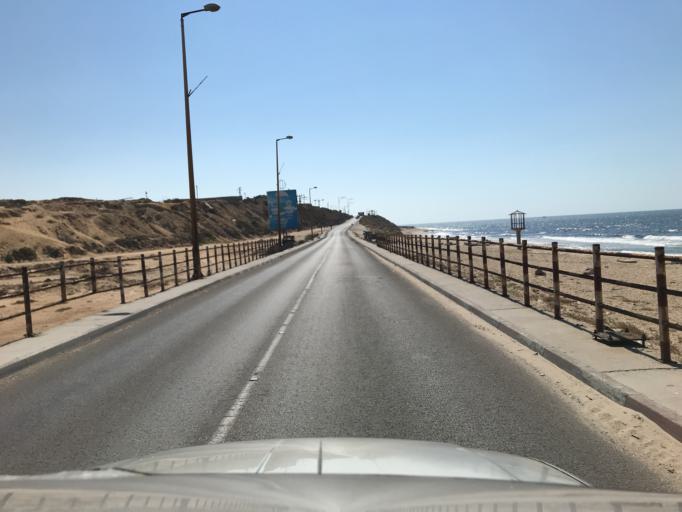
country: PS
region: Gaza Strip
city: An Nusayrat
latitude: 31.4630
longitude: 34.3753
